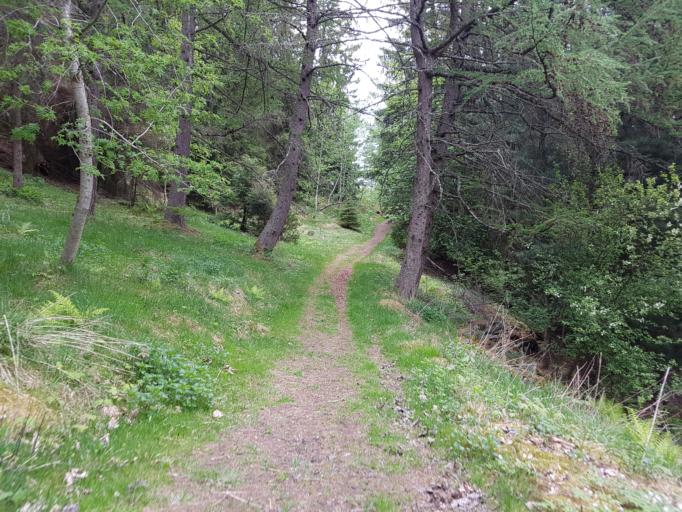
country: NO
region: Nord-Trondelag
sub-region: Levanger
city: Levanger
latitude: 63.7417
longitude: 11.2690
